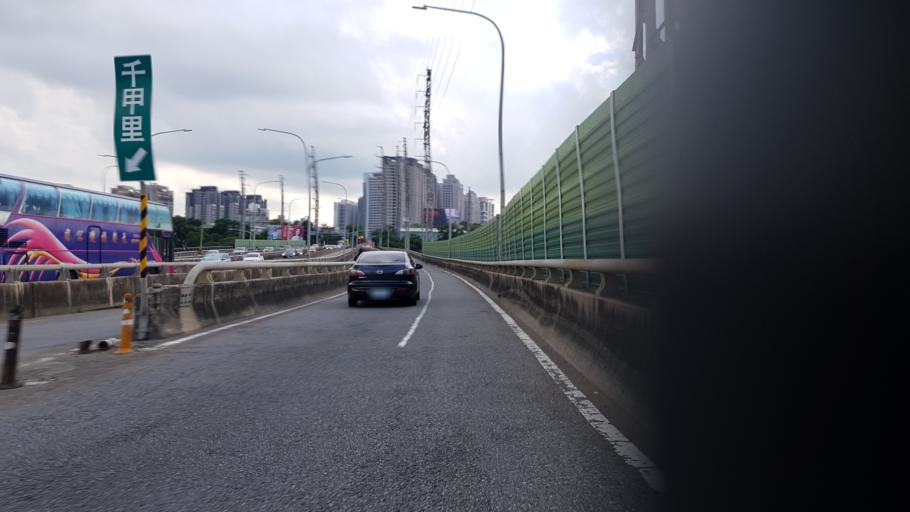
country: TW
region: Taiwan
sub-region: Hsinchu
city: Zhubei
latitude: 24.8009
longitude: 121.0136
